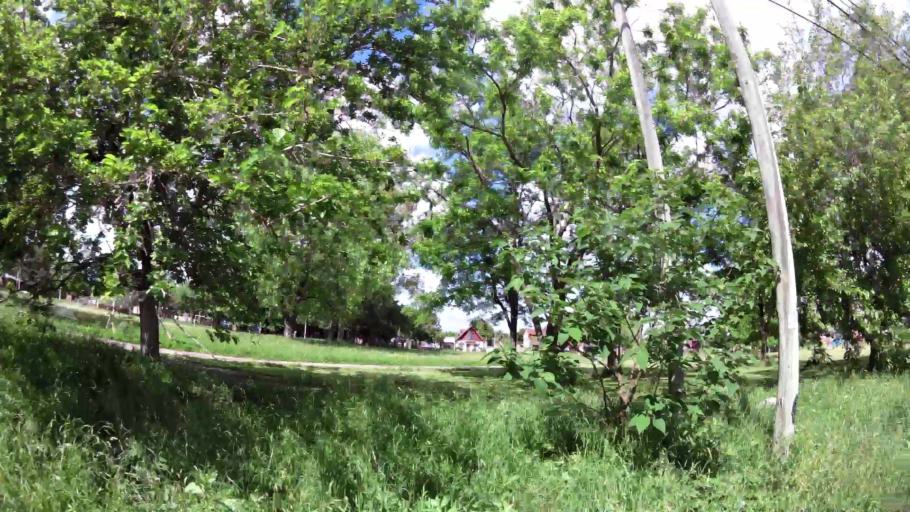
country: AR
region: Buenos Aires
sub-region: Partido de Quilmes
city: Quilmes
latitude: -34.8319
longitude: -58.1756
